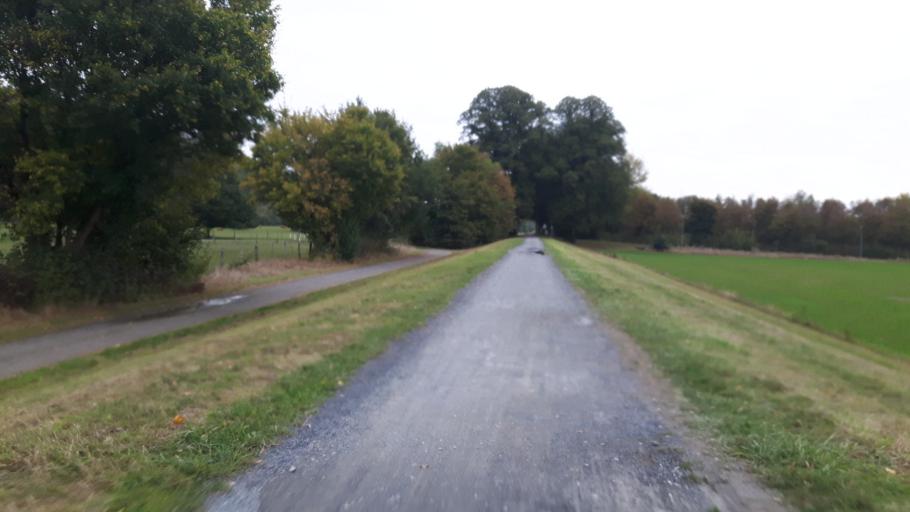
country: DE
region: North Rhine-Westphalia
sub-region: Regierungsbezirk Koln
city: Hennef
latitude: 50.7874
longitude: 7.2803
